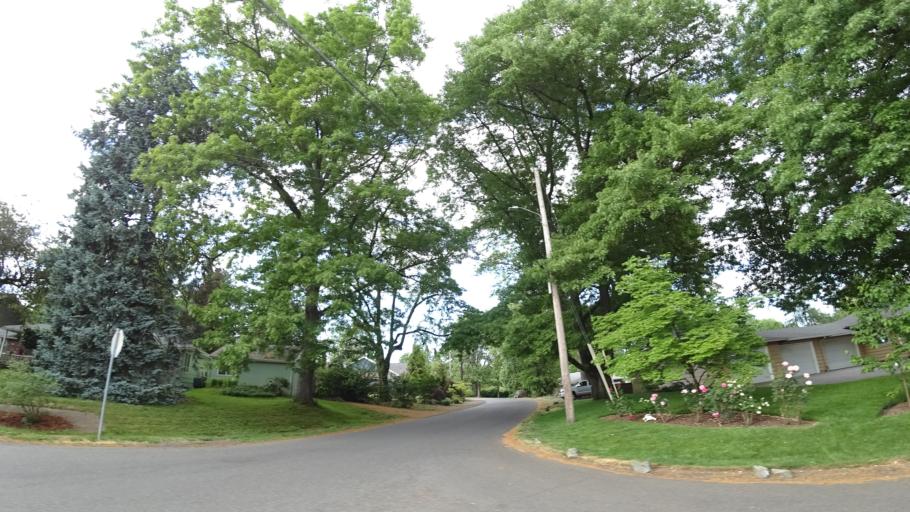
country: US
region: Oregon
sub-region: Washington County
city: Raleigh Hills
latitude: 45.4792
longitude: -122.7339
